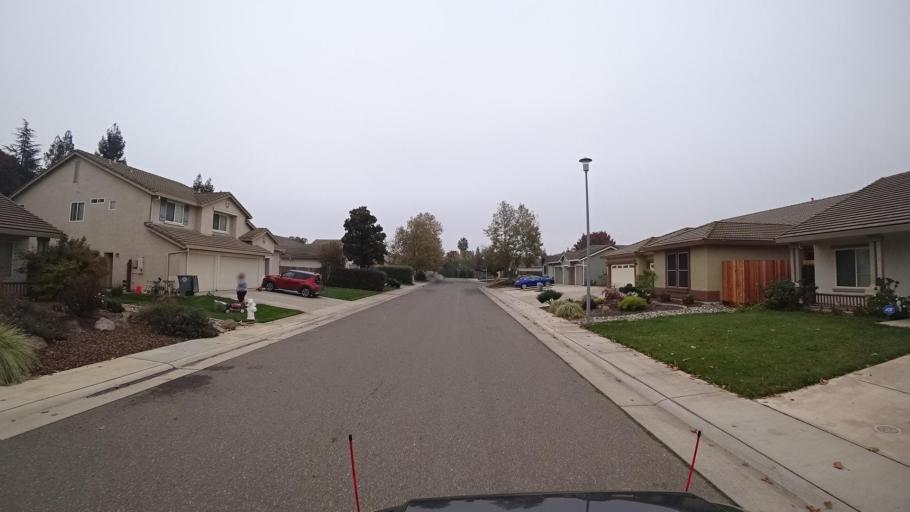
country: US
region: California
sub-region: Sacramento County
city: Elk Grove
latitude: 38.4073
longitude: -121.3434
